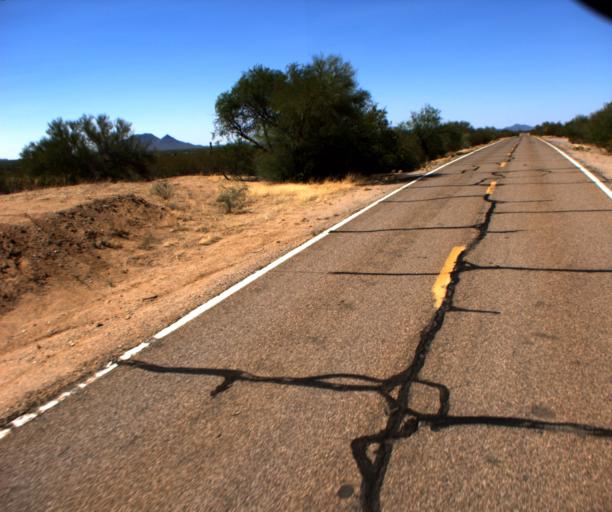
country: US
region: Arizona
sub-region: Pima County
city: Three Points
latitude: 31.9509
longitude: -111.3892
